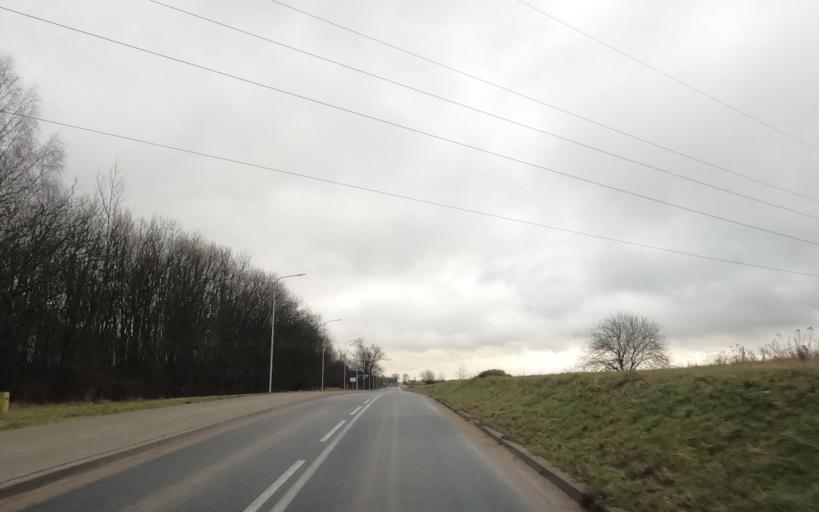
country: PL
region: West Pomeranian Voivodeship
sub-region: Powiat szczecinecki
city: Szczecinek
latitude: 53.7121
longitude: 16.7245
